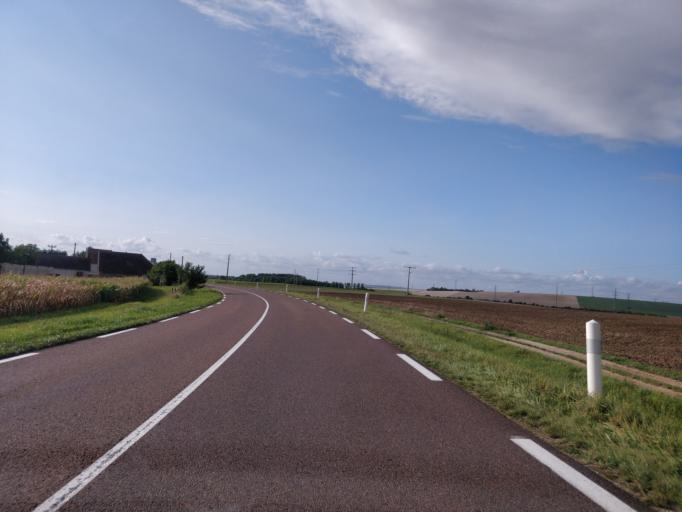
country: FR
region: Champagne-Ardenne
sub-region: Departement de l'Aube
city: Verrieres
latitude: 48.2788
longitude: 4.1967
